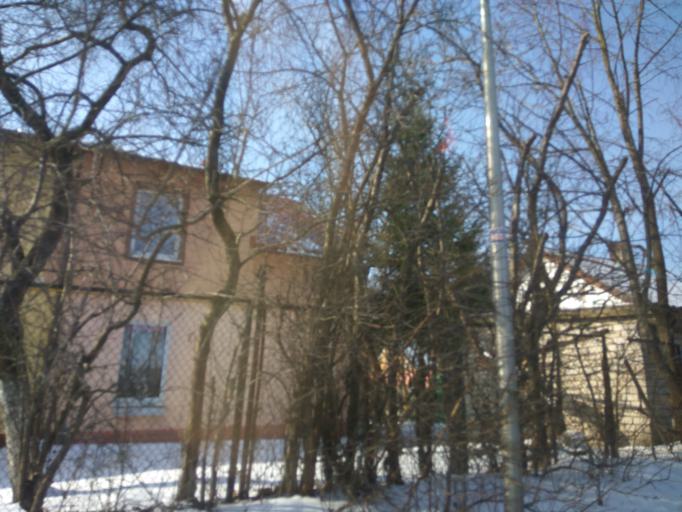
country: RU
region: Kaliningrad
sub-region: Zelenogradskiy Rayon
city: Zelenogradsk
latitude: 54.9586
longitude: 20.4864
